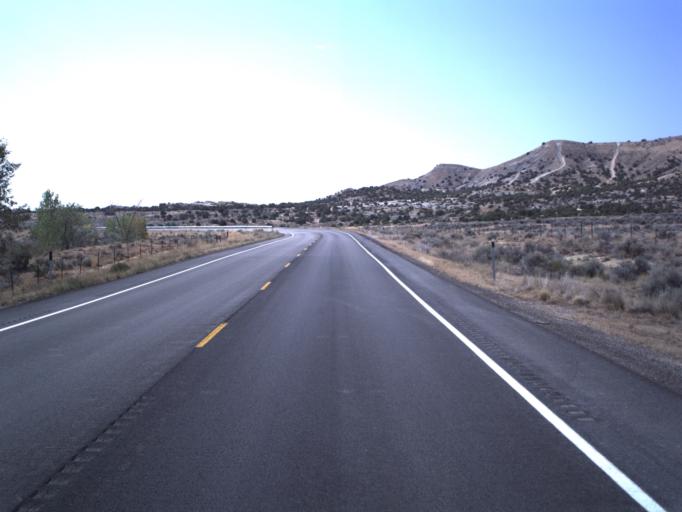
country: US
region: Utah
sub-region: Uintah County
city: Naples
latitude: 40.3591
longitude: -109.4982
